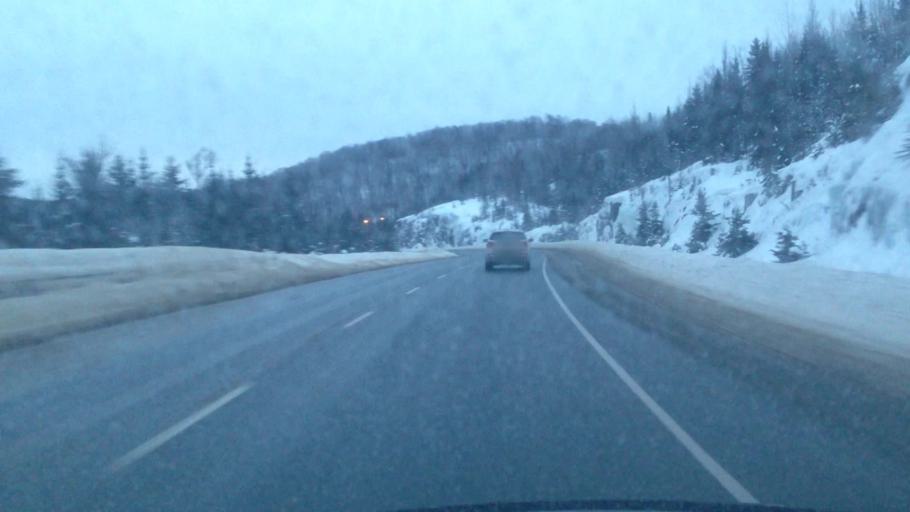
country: CA
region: Quebec
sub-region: Laurentides
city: Sainte-Agathe-des-Monts
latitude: 46.1088
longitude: -74.4182
